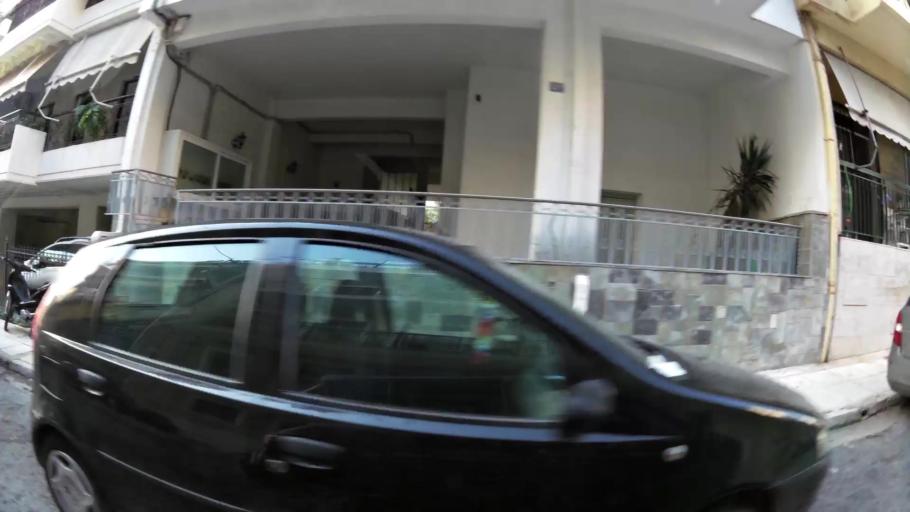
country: GR
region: Attica
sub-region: Nomarchia Athinas
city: Galatsi
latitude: 38.0242
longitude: 23.7494
